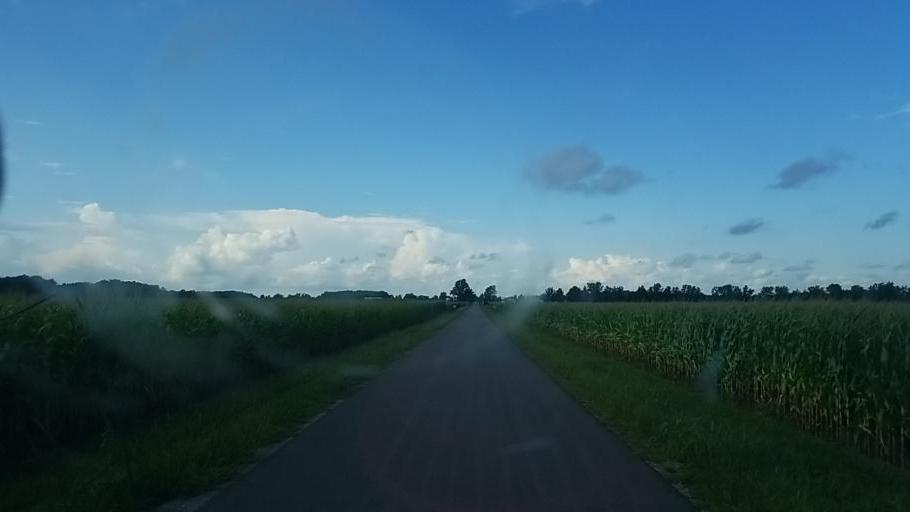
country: US
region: Ohio
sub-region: Hardin County
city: Forest
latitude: 40.7784
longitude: -83.4485
